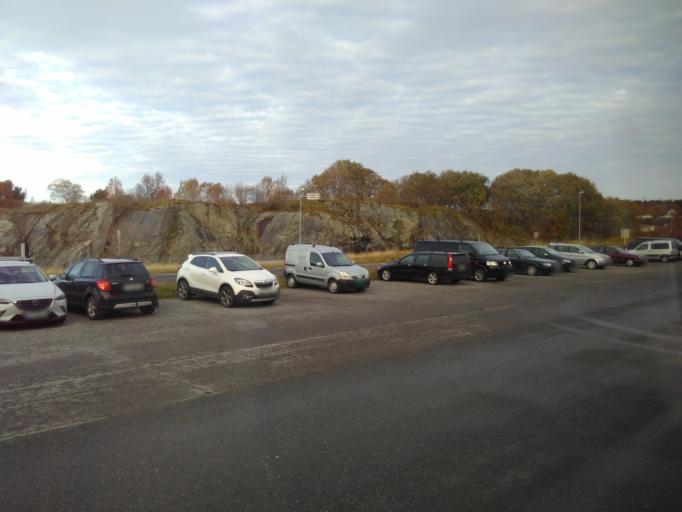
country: NO
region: Sor-Trondelag
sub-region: Hitra
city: Fillan
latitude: 63.5174
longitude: 9.1116
